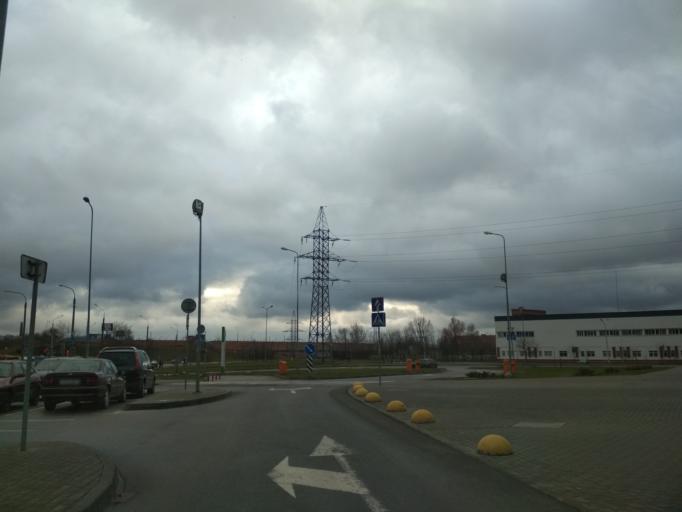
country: BY
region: Minsk
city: Vyaliki Trastsyanets
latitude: 53.8593
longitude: 27.6754
